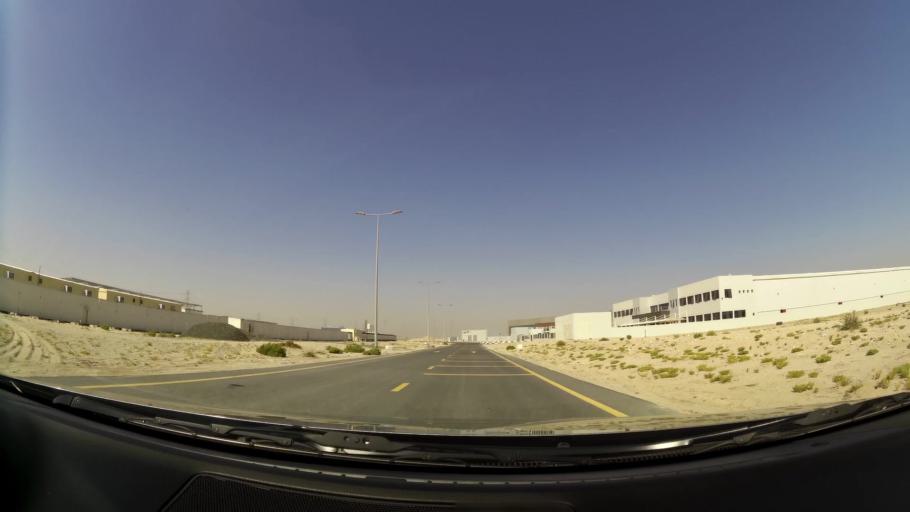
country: AE
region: Dubai
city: Dubai
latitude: 24.9083
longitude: 55.0710
